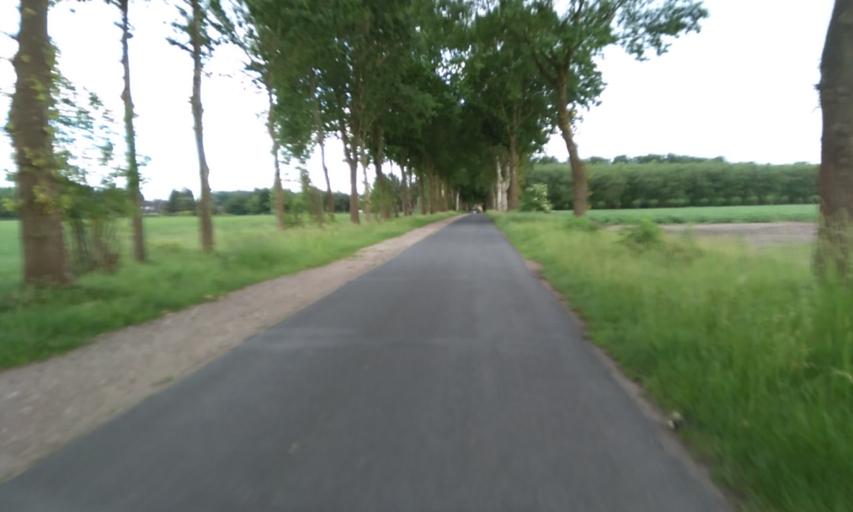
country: DE
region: Lower Saxony
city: Regesbostel
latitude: 53.3856
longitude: 9.6436
